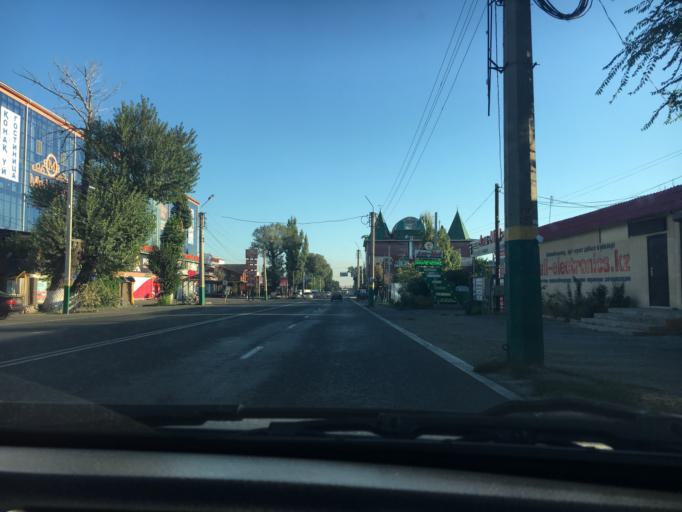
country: KZ
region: Zhambyl
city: Taraz
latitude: 42.8935
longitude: 71.3606
